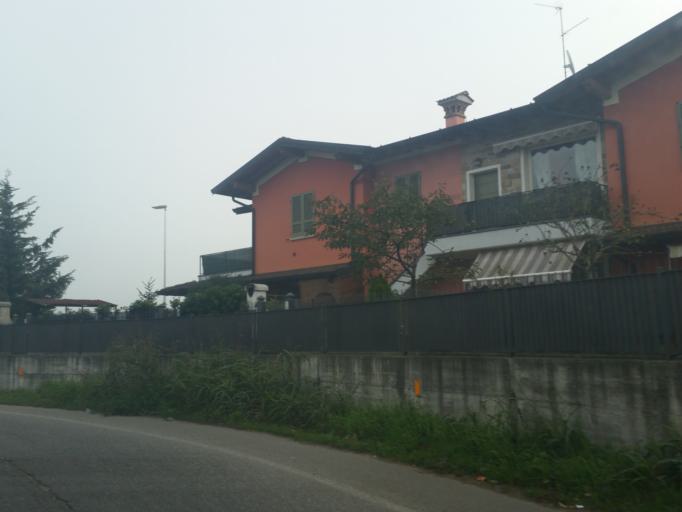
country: IT
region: Lombardy
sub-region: Provincia di Brescia
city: Dello
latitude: 45.4208
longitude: 10.0827
